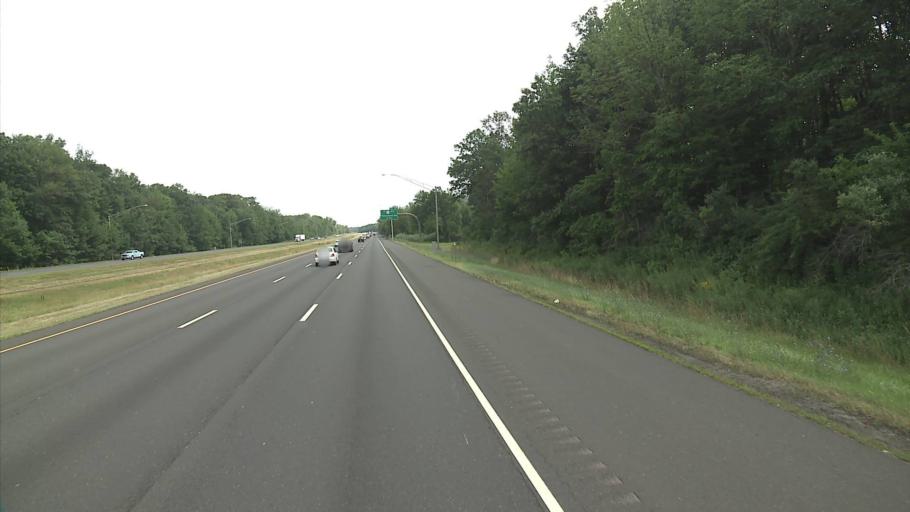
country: US
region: Connecticut
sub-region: Hartford County
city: Farmington
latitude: 41.6934
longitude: -72.8109
